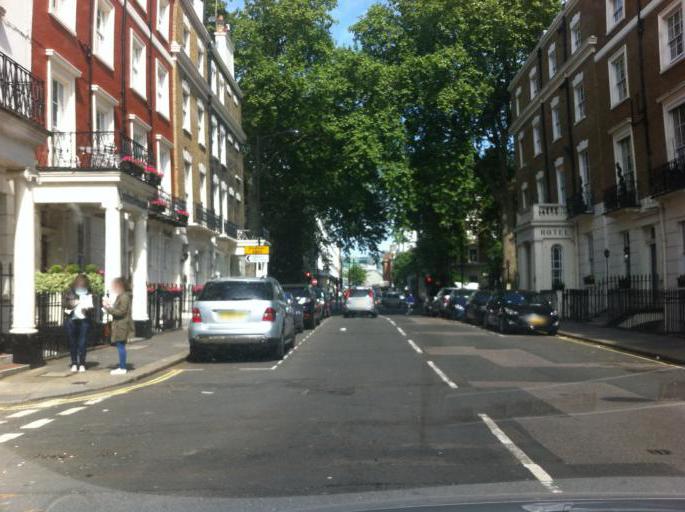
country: GB
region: England
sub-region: Greater London
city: Bayswater
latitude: 51.5144
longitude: -0.1726
